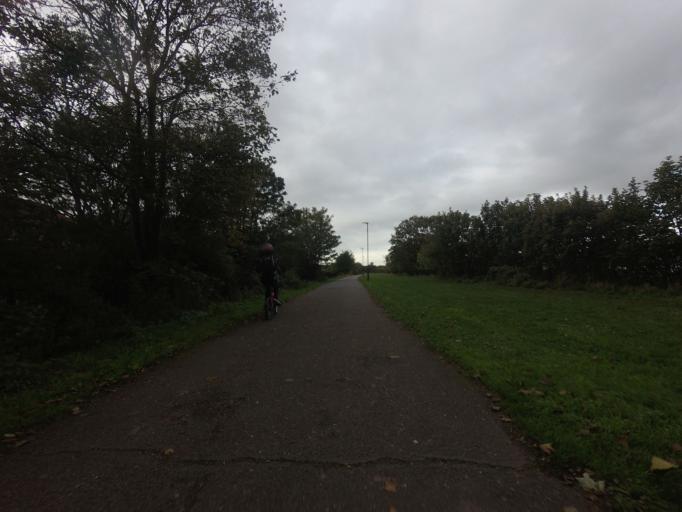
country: GB
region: England
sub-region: Greater London
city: East Ham
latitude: 51.5255
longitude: 0.0236
